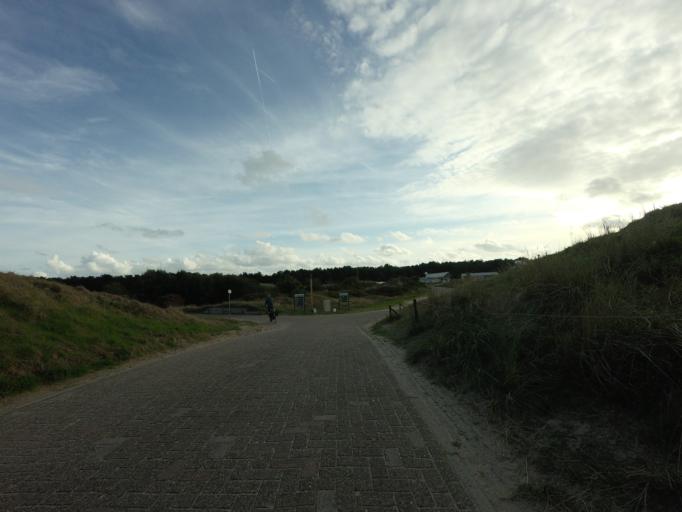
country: NL
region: North Holland
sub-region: Gemeente Den Helder
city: Den Helder
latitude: 53.0207
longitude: 4.7409
